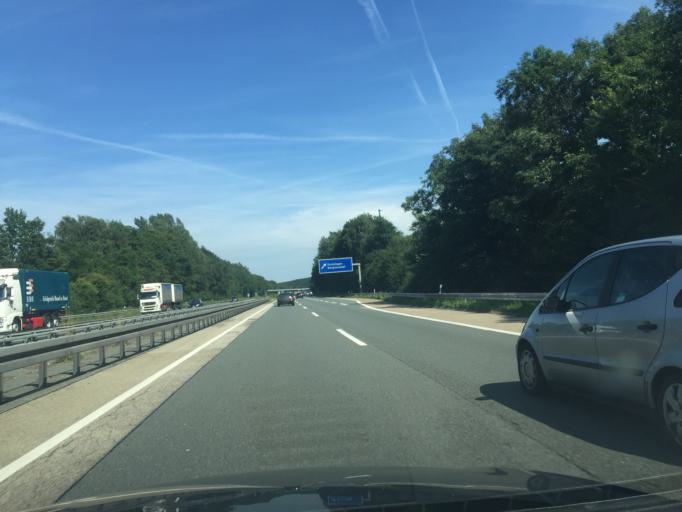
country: DE
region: North Rhine-Westphalia
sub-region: Regierungsbezirk Arnsberg
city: Drolshagen
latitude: 51.0560
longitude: 7.7525
